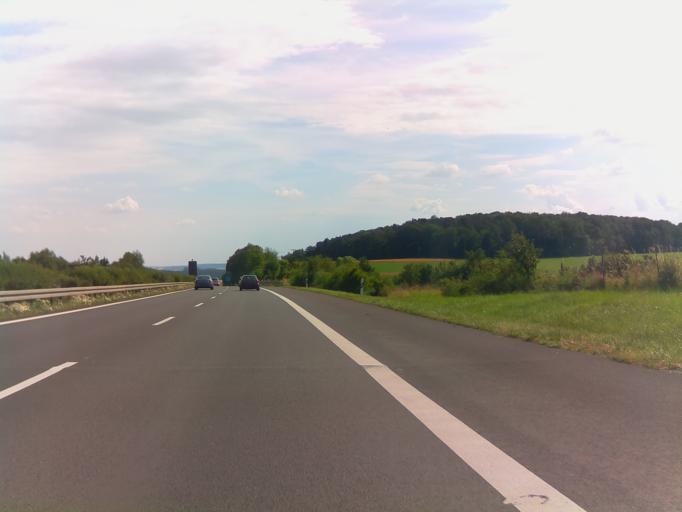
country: DE
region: Bavaria
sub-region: Regierungsbezirk Unterfranken
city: Kleinrinderfeld
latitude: 49.6961
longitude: 9.7918
